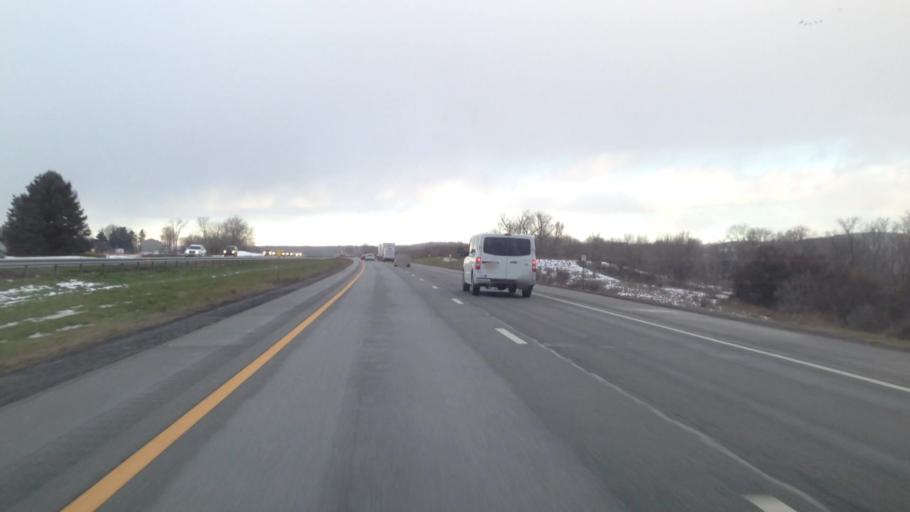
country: US
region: New York
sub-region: Montgomery County
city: Saint Johnsville
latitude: 42.9802
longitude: -74.6567
